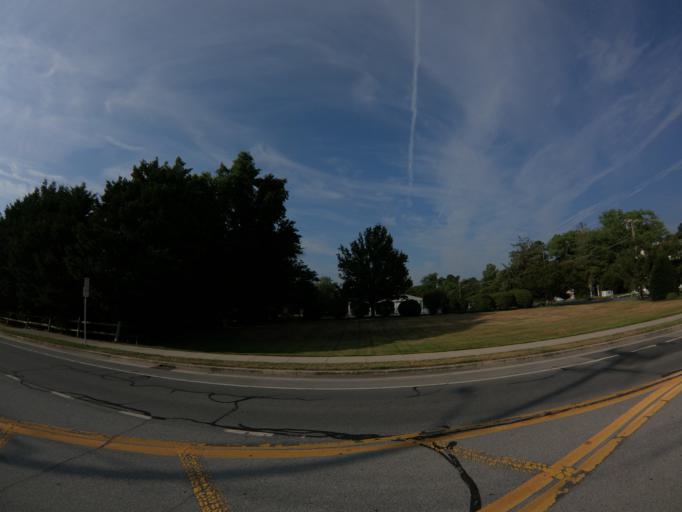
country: US
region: Delaware
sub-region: Sussex County
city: Bethany Beach
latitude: 38.5398
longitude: -75.0675
